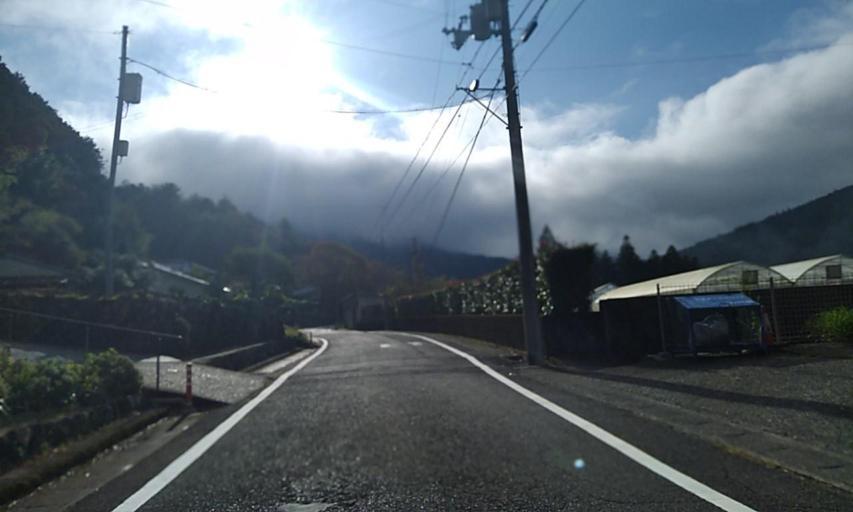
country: JP
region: Wakayama
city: Shingu
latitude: 33.9264
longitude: 135.9820
